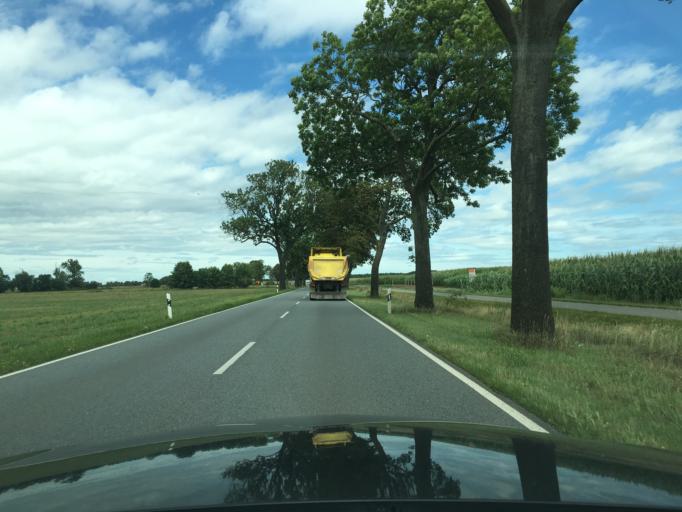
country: DE
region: Brandenburg
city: Gransee
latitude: 52.8784
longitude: 13.1620
